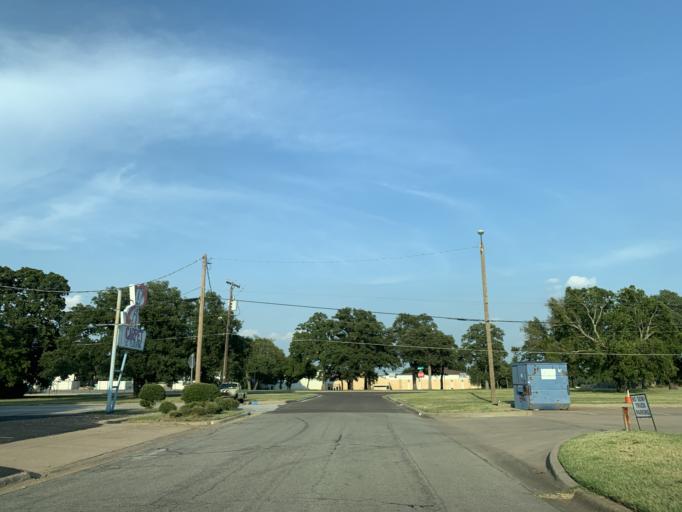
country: US
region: Texas
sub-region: Tarrant County
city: Hurst
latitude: 32.8100
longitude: -97.1700
